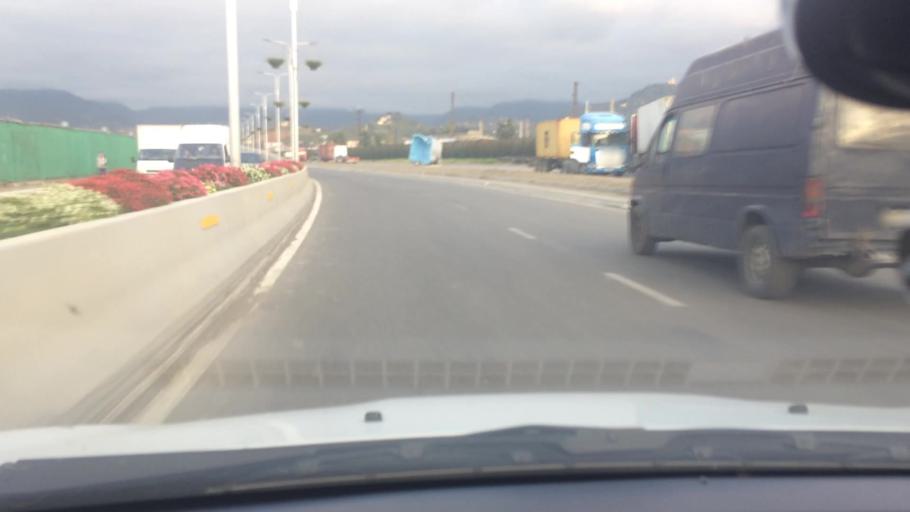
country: GE
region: Ajaria
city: Batumi
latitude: 41.6461
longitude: 41.6534
